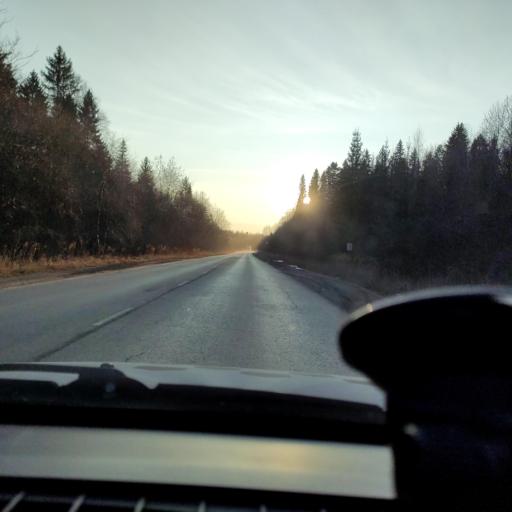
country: RU
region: Perm
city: Ferma
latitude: 57.9619
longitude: 56.3473
